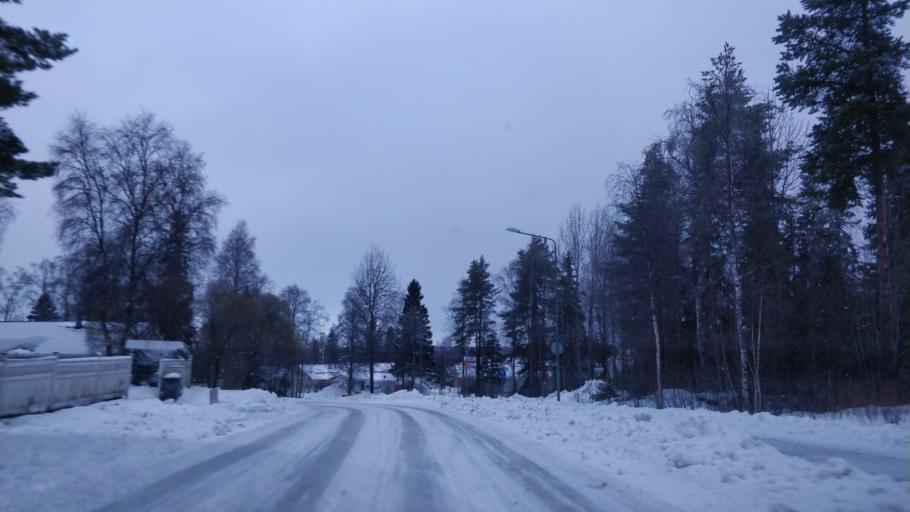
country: FI
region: Lapland
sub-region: Kemi-Tornio
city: Kemi
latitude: 65.7431
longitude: 24.5988
